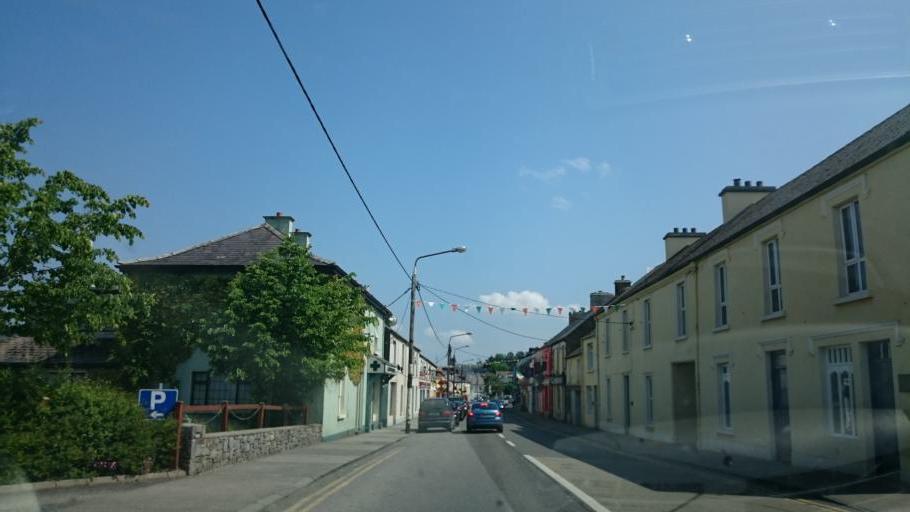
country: IE
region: Connaught
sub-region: Sligo
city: Tobercurry
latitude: 54.0526
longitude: -8.7321
